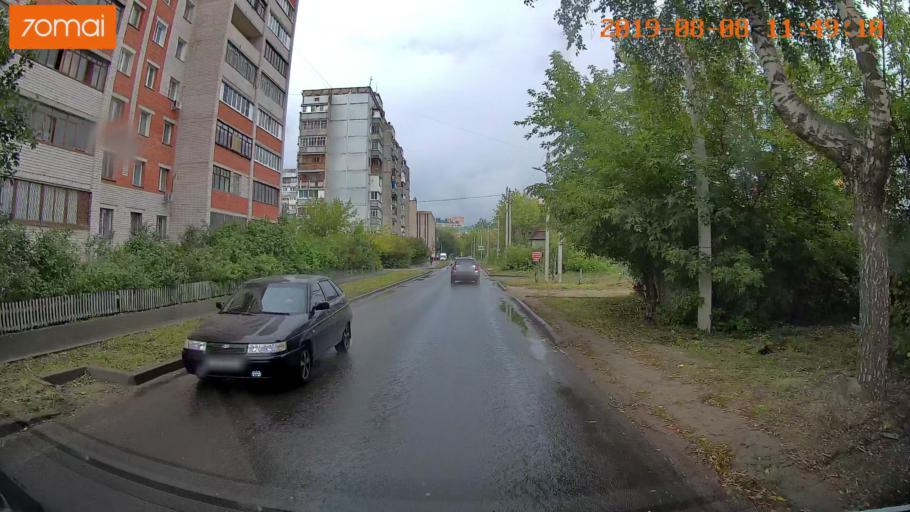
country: RU
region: Ivanovo
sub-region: Gorod Ivanovo
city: Ivanovo
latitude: 56.9760
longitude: 40.9829
